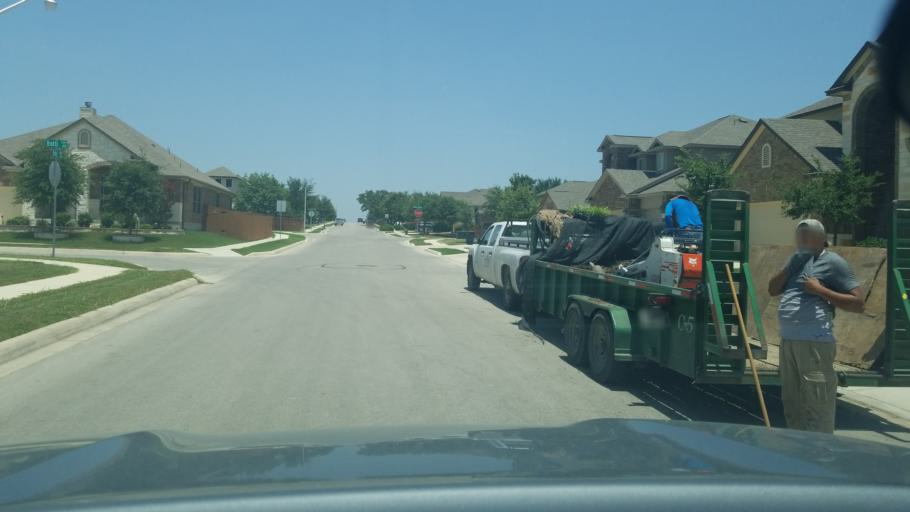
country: US
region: Texas
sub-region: Guadalupe County
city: Cibolo
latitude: 29.5787
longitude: -98.2311
